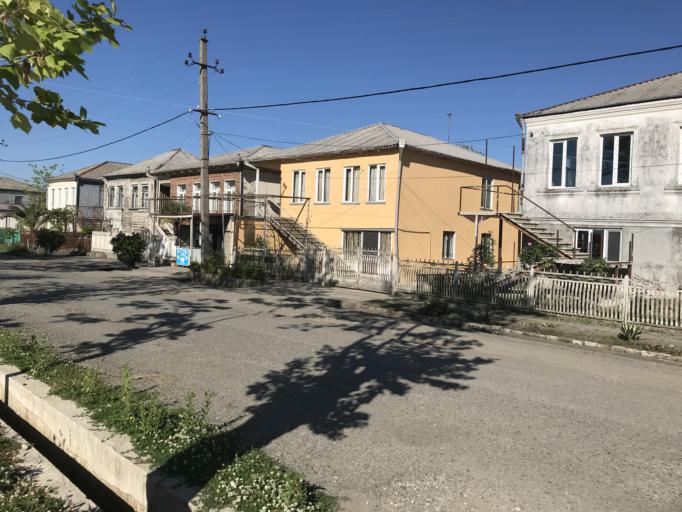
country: GE
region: Samegrelo and Zemo Svaneti
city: P'ot'i
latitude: 42.1352
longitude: 41.6692
